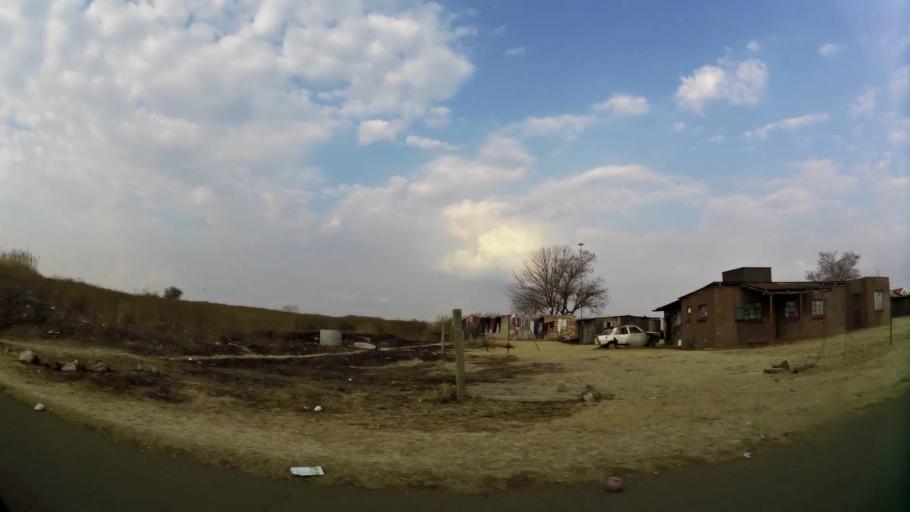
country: ZA
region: Gauteng
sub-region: Sedibeng District Municipality
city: Vanderbijlpark
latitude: -26.6888
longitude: 27.8804
